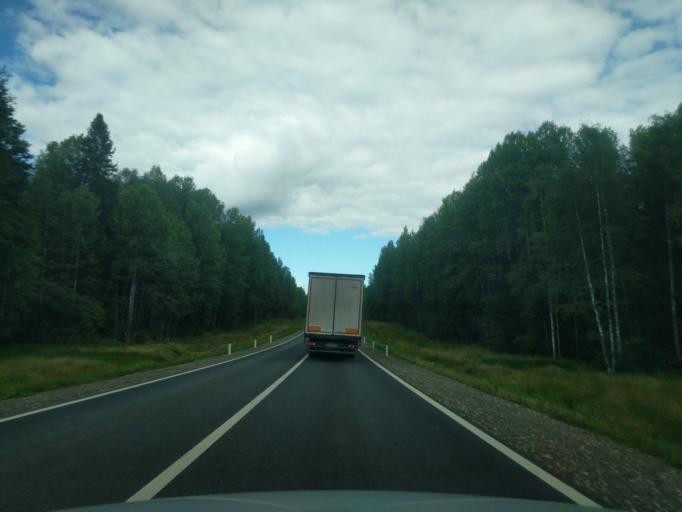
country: RU
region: Kostroma
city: Kadyy
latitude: 57.8472
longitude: 43.4674
